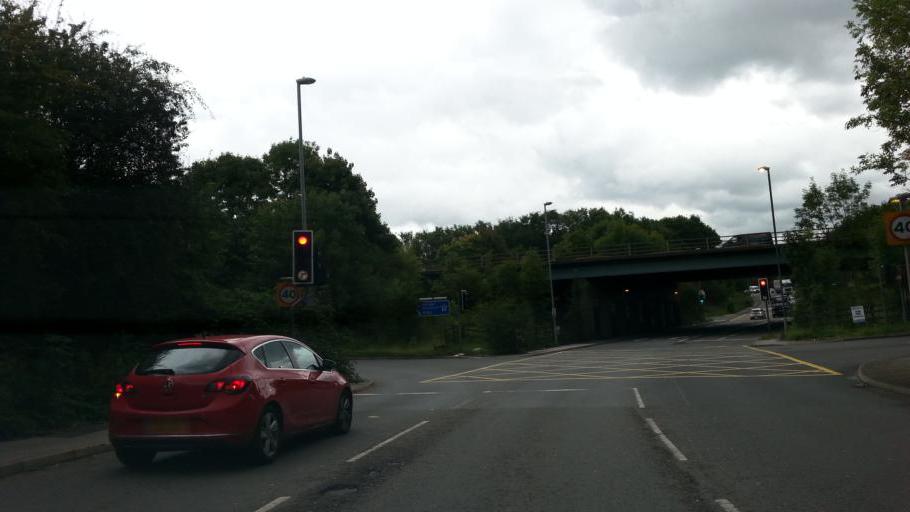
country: GB
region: England
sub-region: Borough of Bury
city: Bury
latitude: 53.5788
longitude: -2.2728
